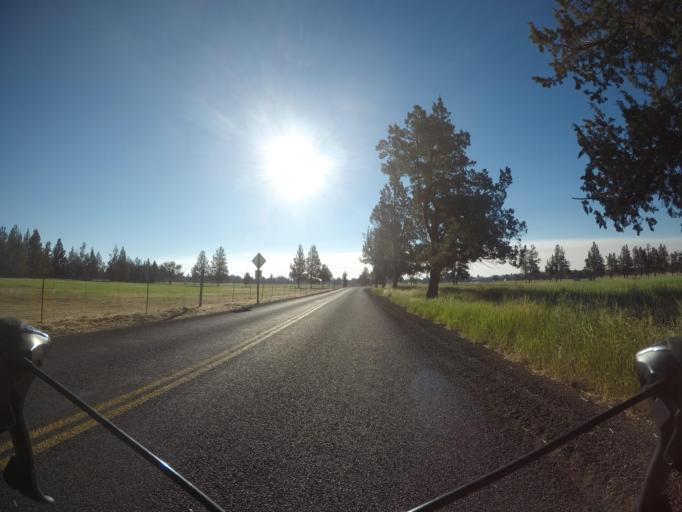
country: US
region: Oregon
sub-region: Deschutes County
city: Redmond
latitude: 44.2658
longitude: -121.2466
